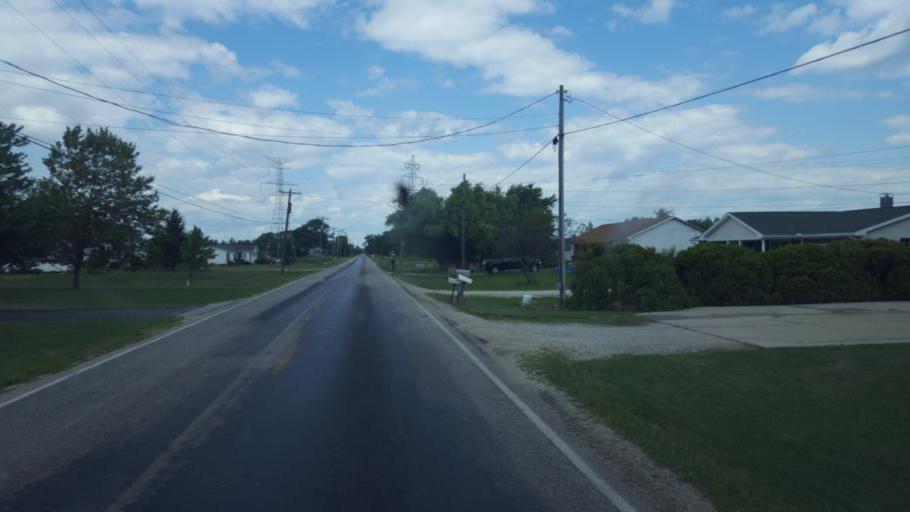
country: US
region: Ohio
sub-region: Lucas County
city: Curtice
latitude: 41.6052
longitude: -83.2794
